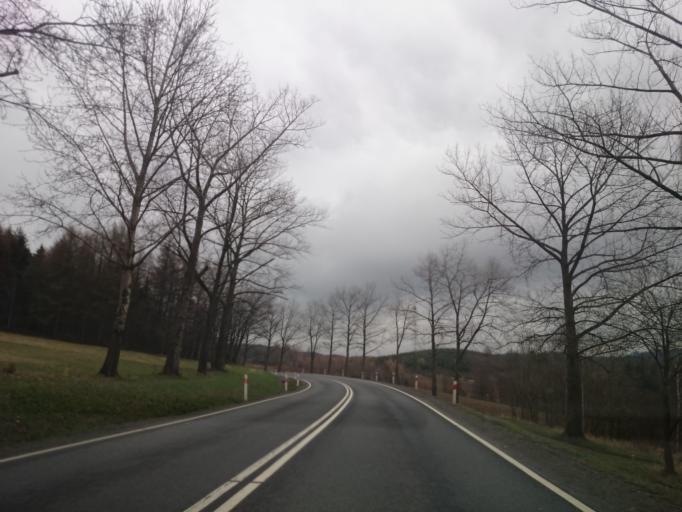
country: PL
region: Lower Silesian Voivodeship
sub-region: Powiat zabkowicki
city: Bardo
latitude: 50.4313
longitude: 16.7568
